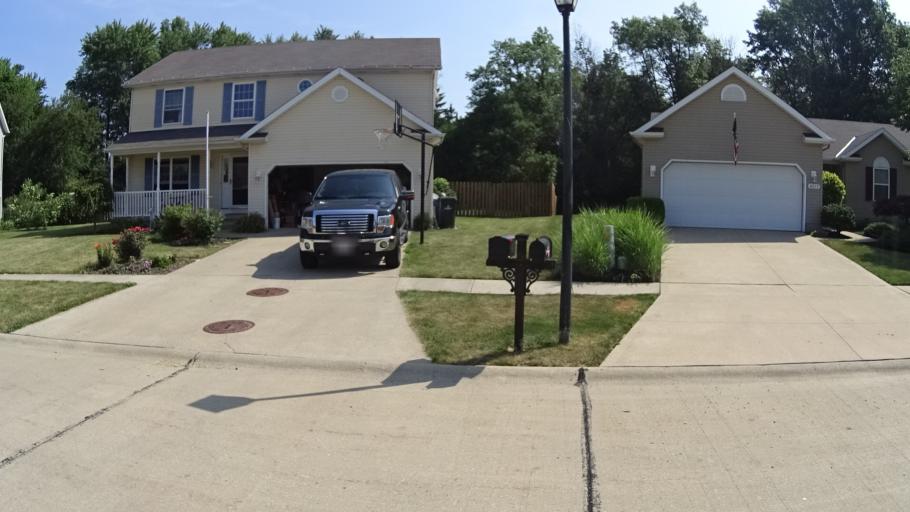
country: US
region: Ohio
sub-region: Lorain County
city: Vermilion
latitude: 41.4152
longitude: -82.3738
